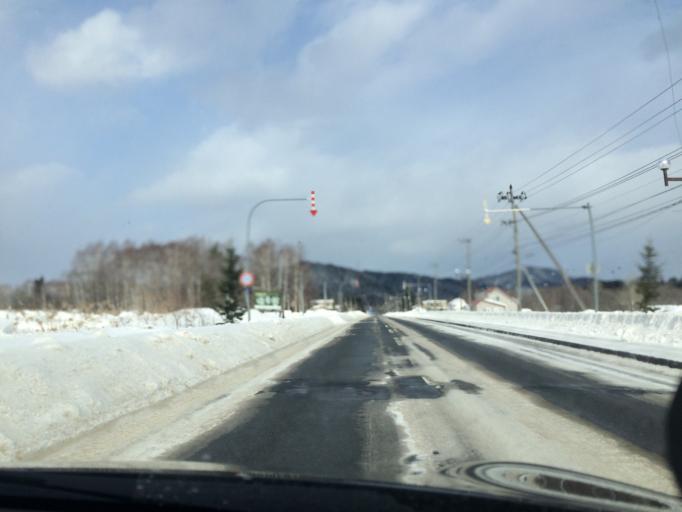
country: JP
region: Hokkaido
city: Shimo-furano
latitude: 42.9970
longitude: 142.4038
